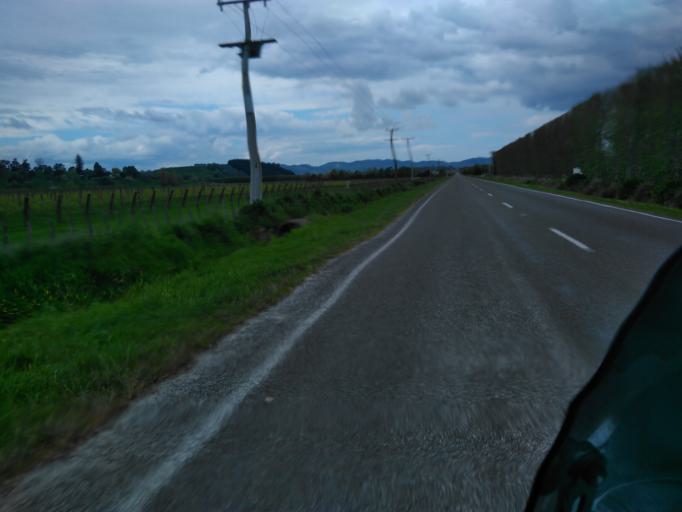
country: NZ
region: Gisborne
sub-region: Gisborne District
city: Gisborne
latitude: -38.6441
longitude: 177.8702
